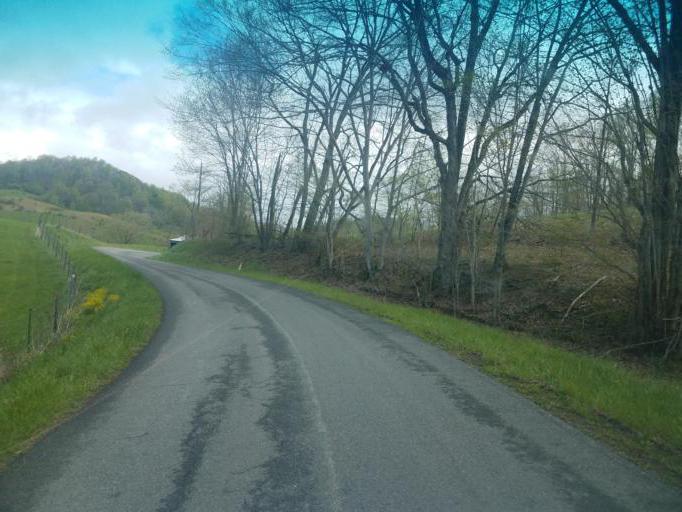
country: US
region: Virginia
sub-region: Smyth County
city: Atkins
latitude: 36.9752
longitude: -81.3969
